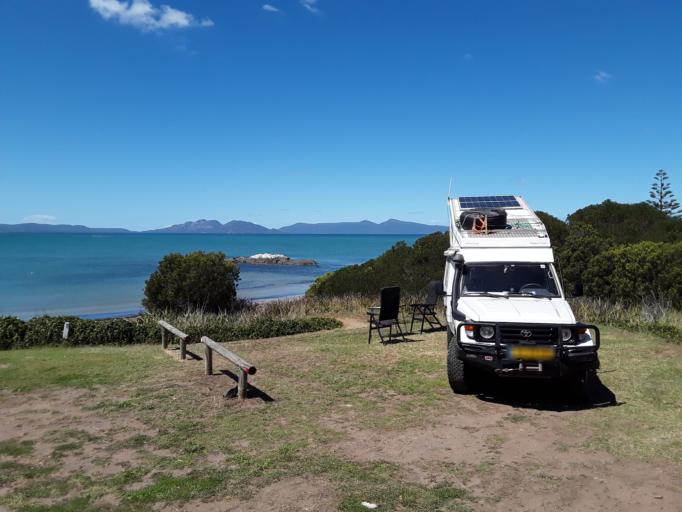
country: AU
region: Tasmania
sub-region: Break O'Day
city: St Helens
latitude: -42.1189
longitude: 148.0733
